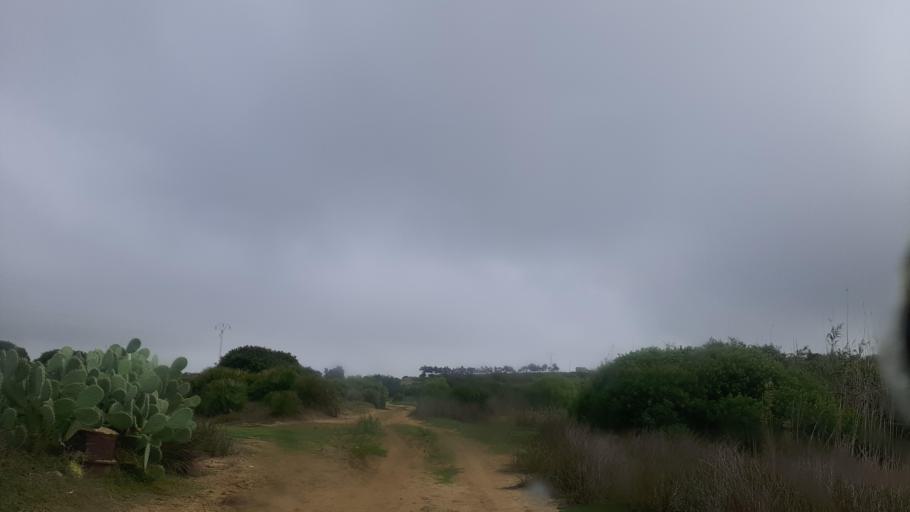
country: TN
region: Nabul
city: Qulaybiyah
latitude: 36.8251
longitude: 11.0378
